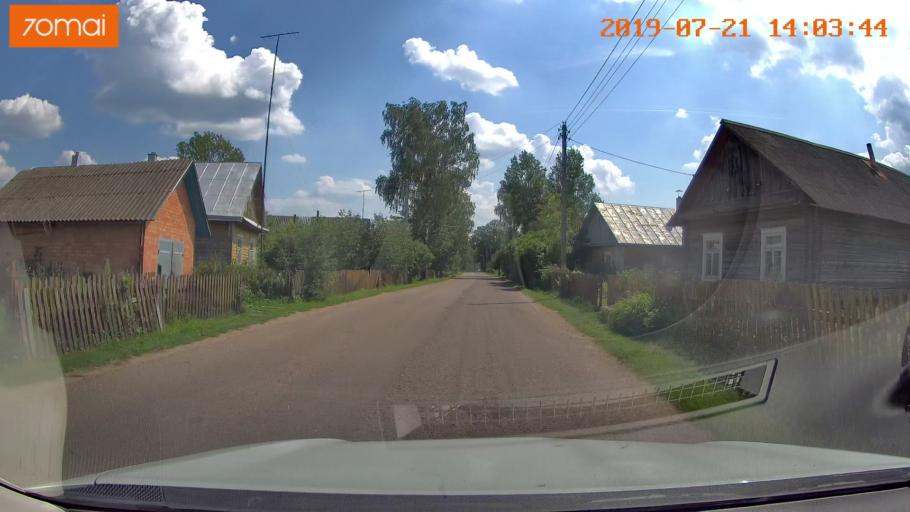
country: BY
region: Grodnenskaya
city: Lyubcha
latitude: 53.7267
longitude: 26.0933
